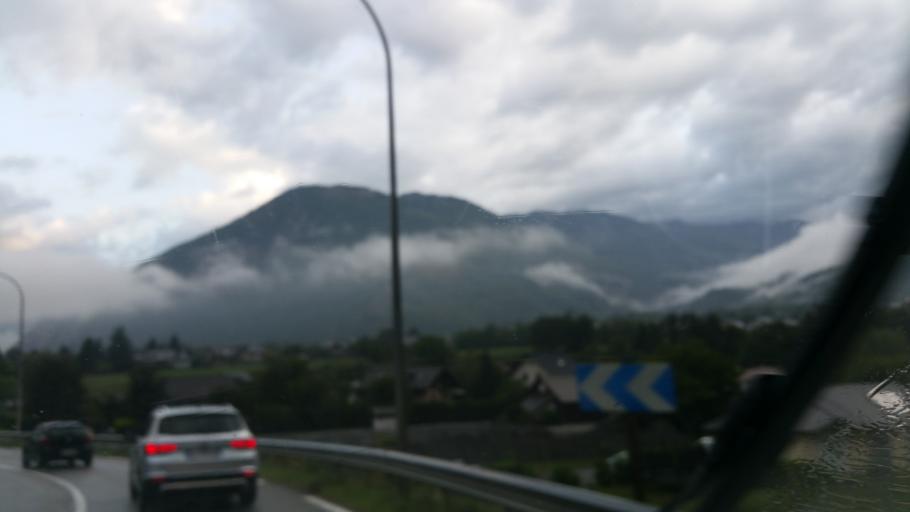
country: FR
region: Rhone-Alpes
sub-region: Departement de la Savoie
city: La Chambre
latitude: 45.3501
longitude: 6.3066
